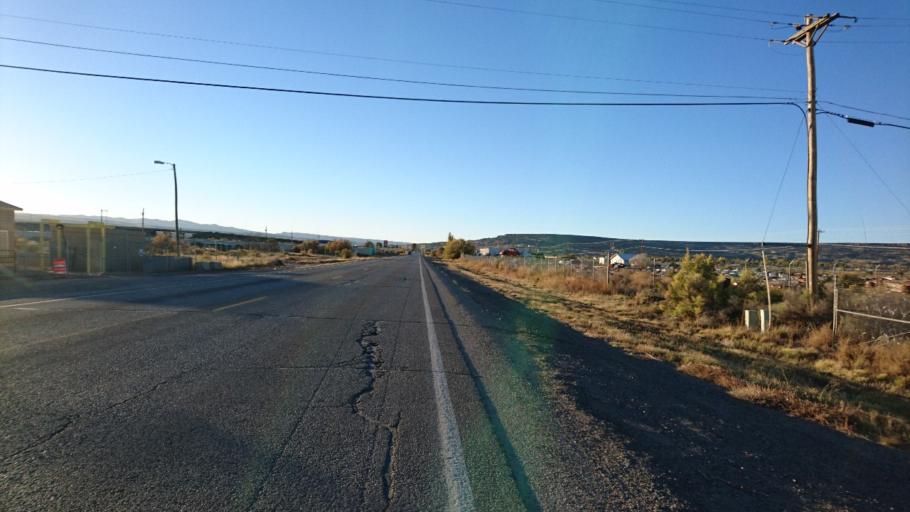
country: US
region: New Mexico
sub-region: Cibola County
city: Grants
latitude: 35.1366
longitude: -107.8221
